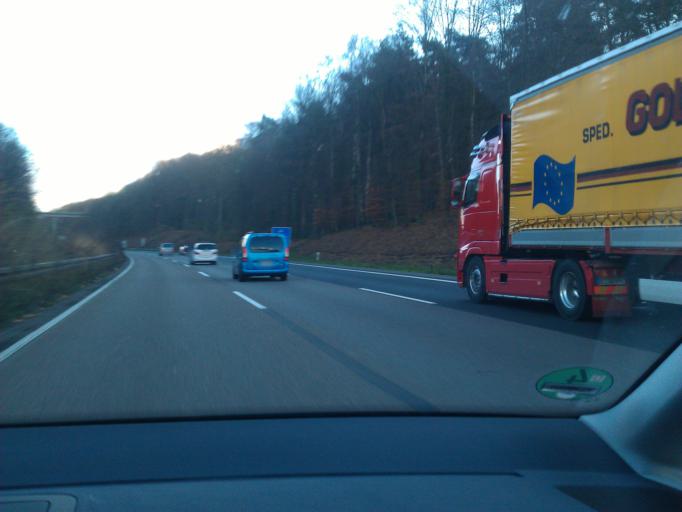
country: DE
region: North Rhine-Westphalia
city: Herdecke
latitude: 51.4468
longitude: 7.4292
